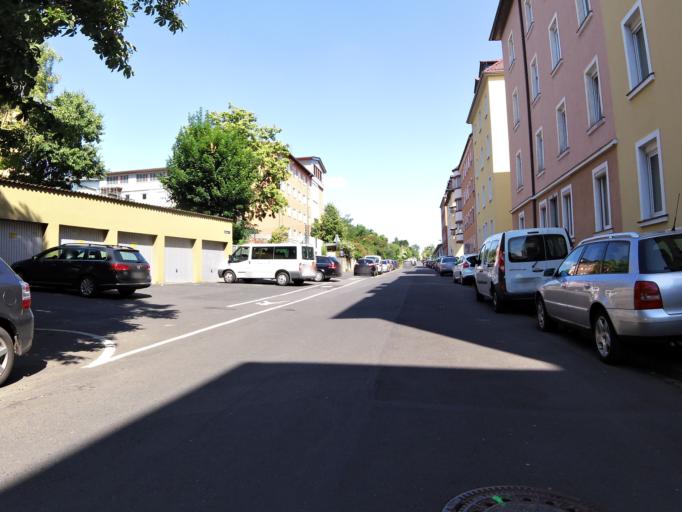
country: DE
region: Bavaria
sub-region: Regierungsbezirk Unterfranken
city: Wuerzburg
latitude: 49.8046
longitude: 9.9430
